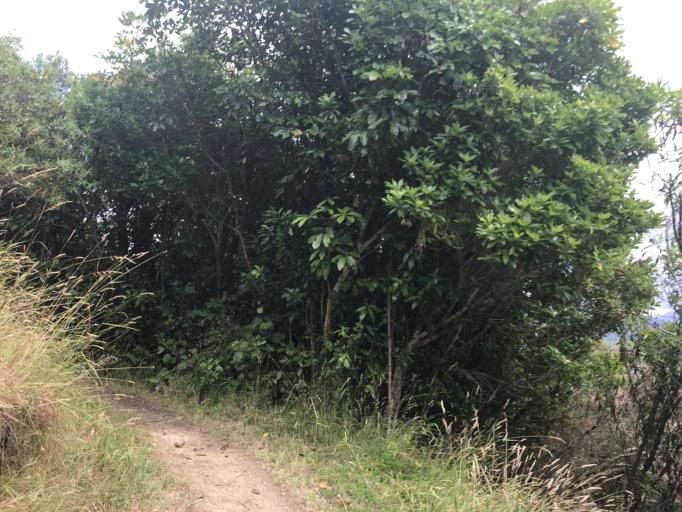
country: NZ
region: Marlborough
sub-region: Marlborough District
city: Picton
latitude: -41.2149
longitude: 173.9798
